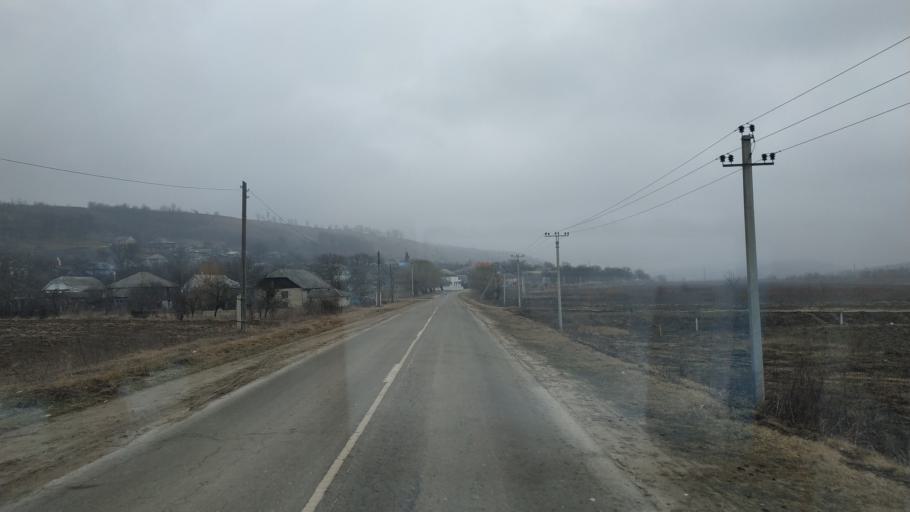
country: MD
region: Hincesti
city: Hincesti
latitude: 46.9571
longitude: 28.4901
